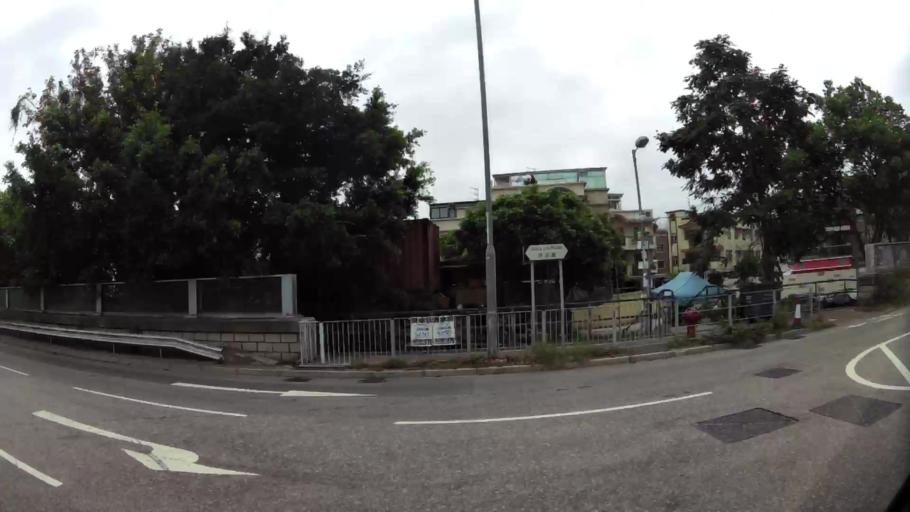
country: HK
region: Yuen Long
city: Yuen Long Kau Hui
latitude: 22.4390
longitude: 113.9962
